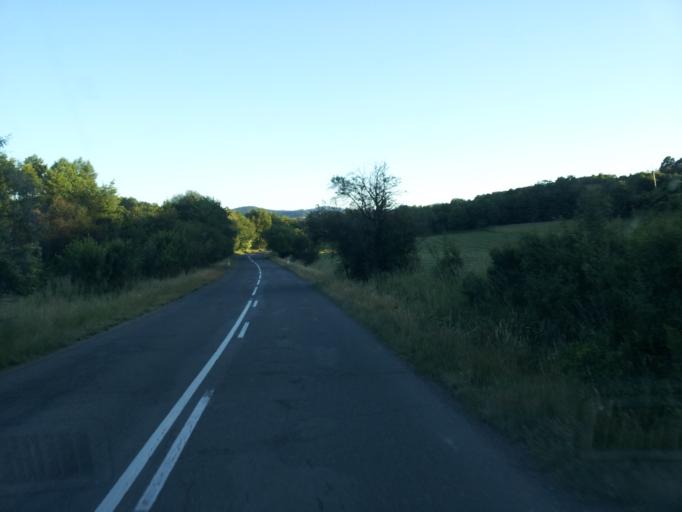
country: SK
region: Banskobystricky
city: Svaety Anton
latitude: 48.3765
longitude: 18.9238
